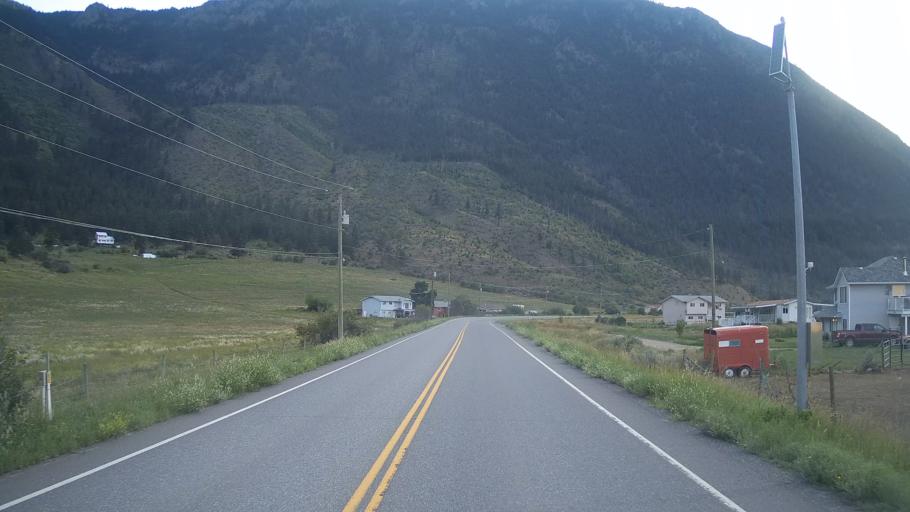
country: CA
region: British Columbia
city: Lillooet
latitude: 50.7421
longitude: -121.8800
